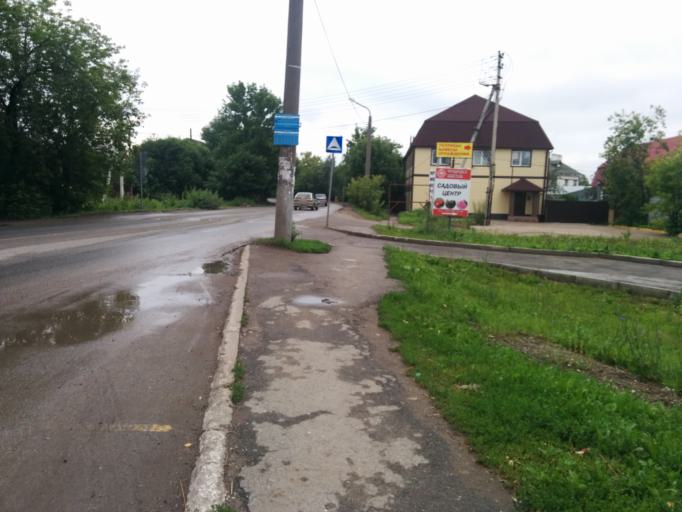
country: RU
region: Perm
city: Perm
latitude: 57.9862
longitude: 56.3043
